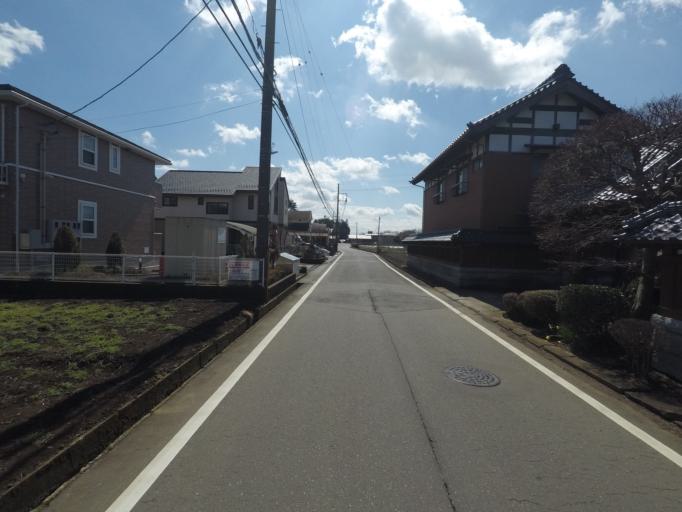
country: JP
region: Ibaraki
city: Naka
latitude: 36.0478
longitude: 140.1111
